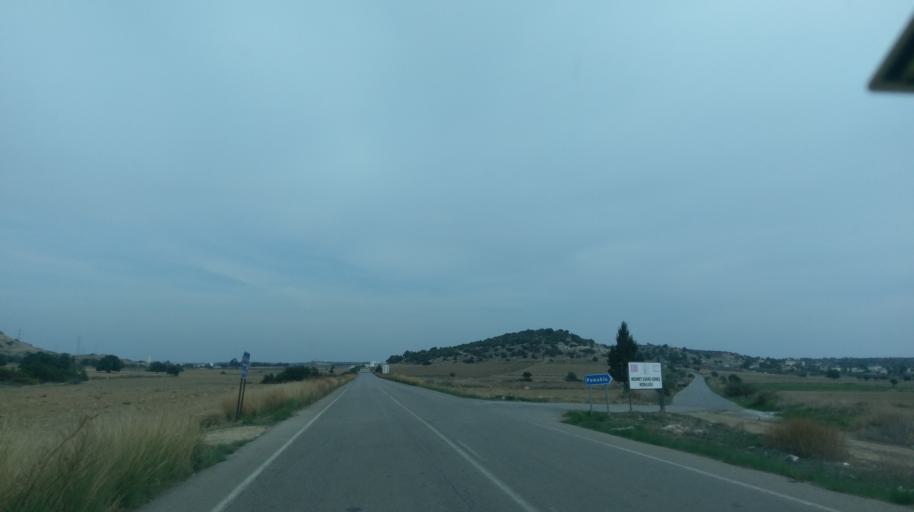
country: CY
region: Ammochostos
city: Leonarisso
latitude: 35.3966
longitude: 34.0662
